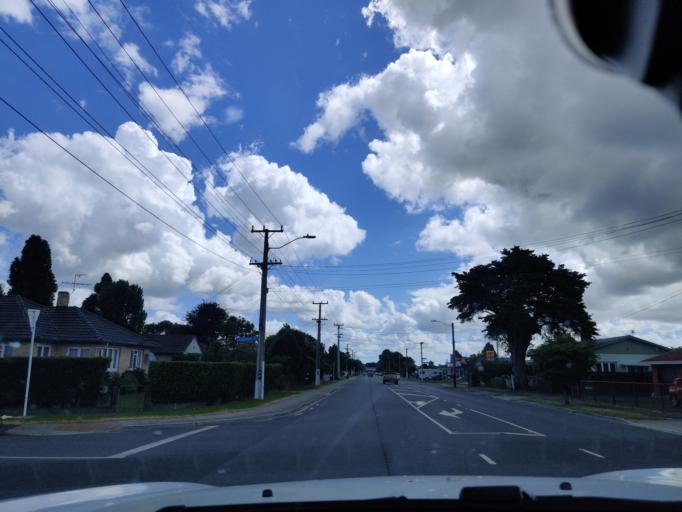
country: NZ
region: Auckland
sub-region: Auckland
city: Papakura
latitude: -37.0579
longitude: 174.9545
